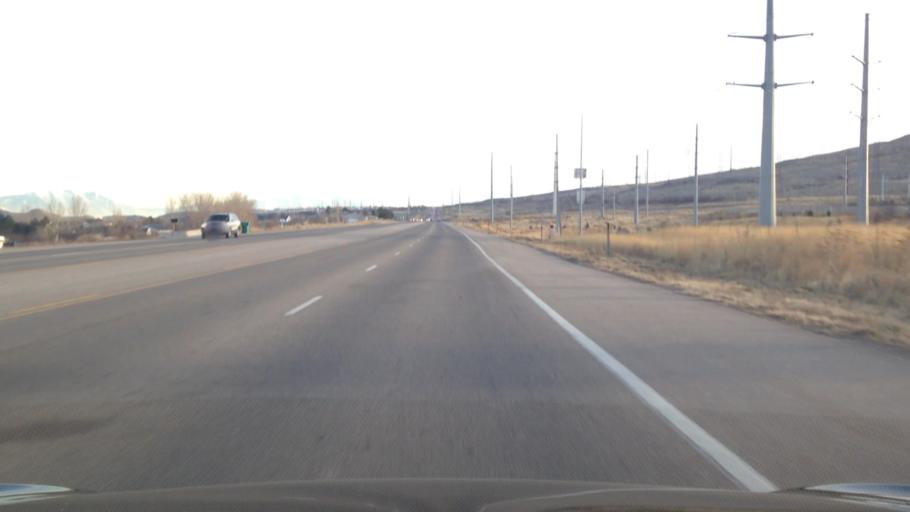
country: US
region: Utah
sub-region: Salt Lake County
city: Bluffdale
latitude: 40.4701
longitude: -111.9464
